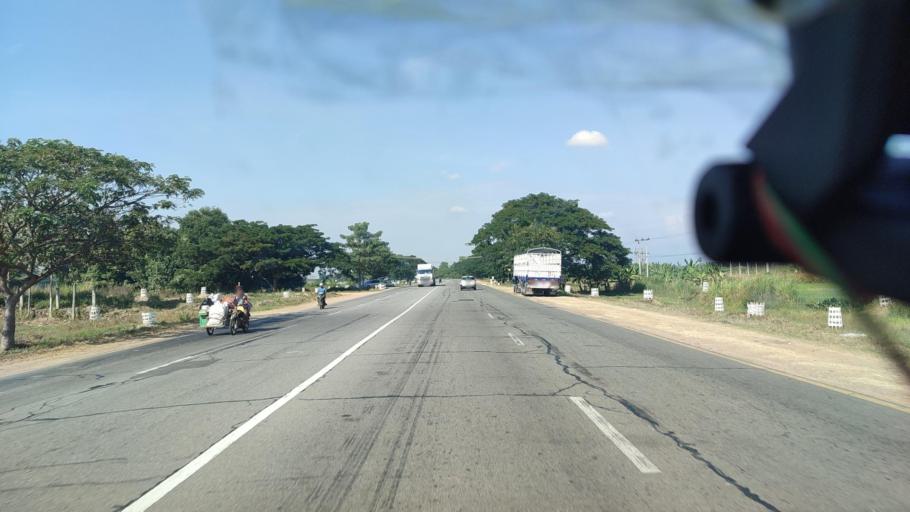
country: MM
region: Mandalay
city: Pyinmana
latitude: 19.6135
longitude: 96.2517
